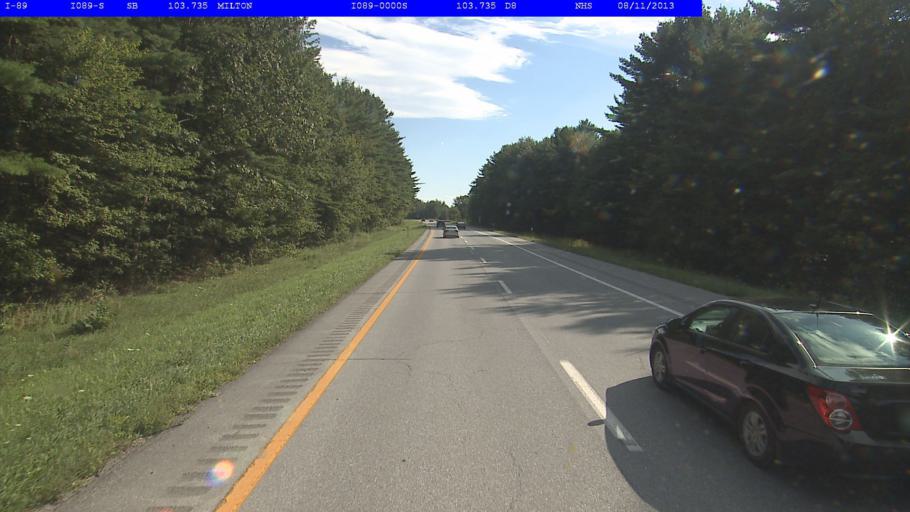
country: US
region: Vermont
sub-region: Chittenden County
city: Milton
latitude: 44.6670
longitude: -73.1359
